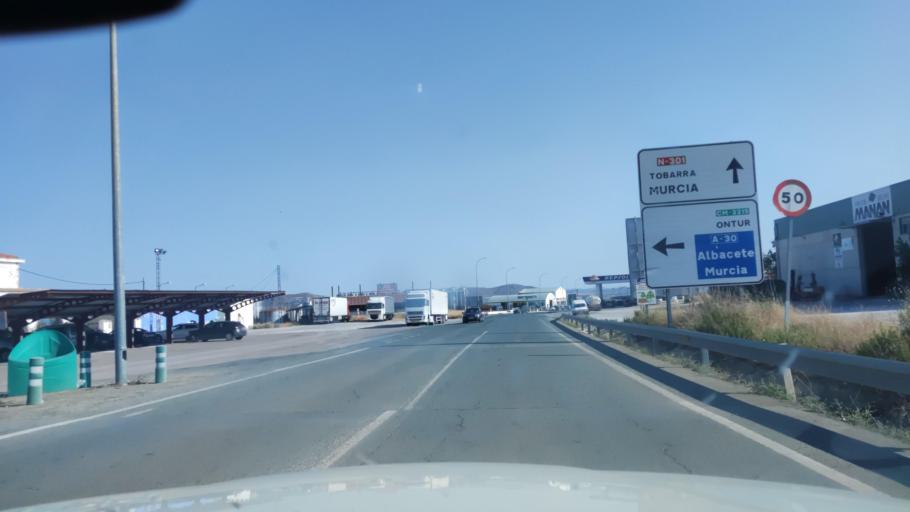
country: ES
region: Castille-La Mancha
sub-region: Provincia de Albacete
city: Tobarra
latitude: 38.6037
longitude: -1.6811
